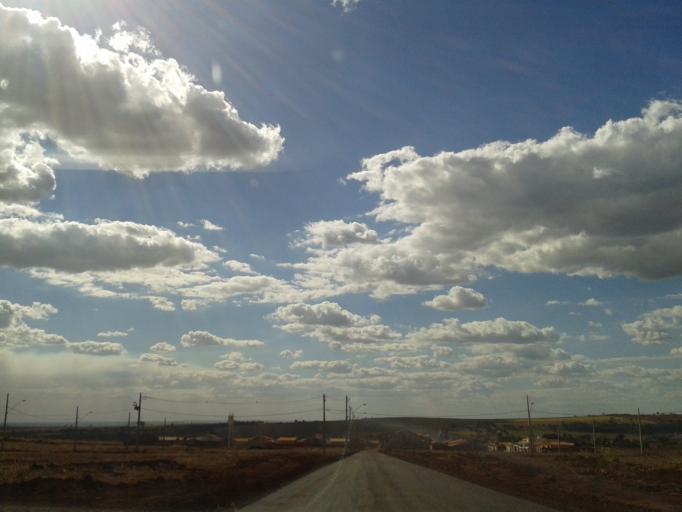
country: BR
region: Minas Gerais
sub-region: Capinopolis
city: Capinopolis
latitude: -18.6962
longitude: -49.5762
